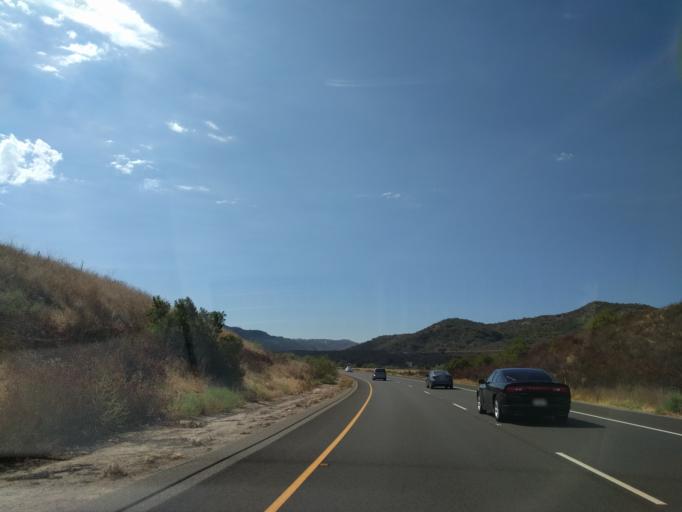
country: US
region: California
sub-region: Orange County
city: Laguna Woods
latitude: 33.6026
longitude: -117.7630
